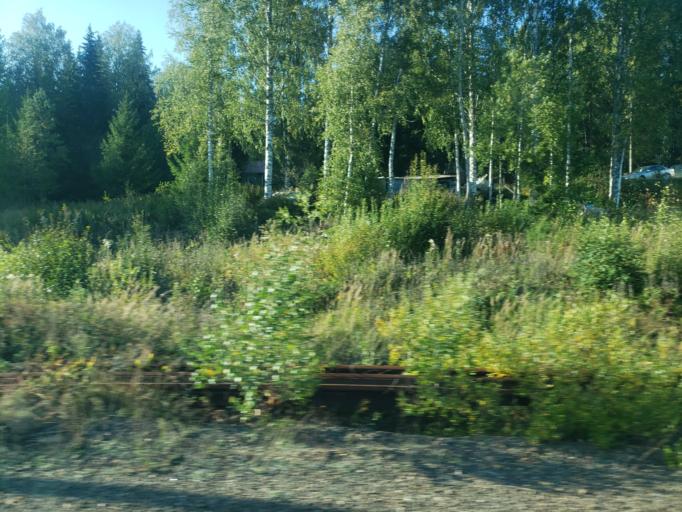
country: FI
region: South Karelia
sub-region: Lappeenranta
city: Lappeenranta
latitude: 60.9099
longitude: 28.1632
